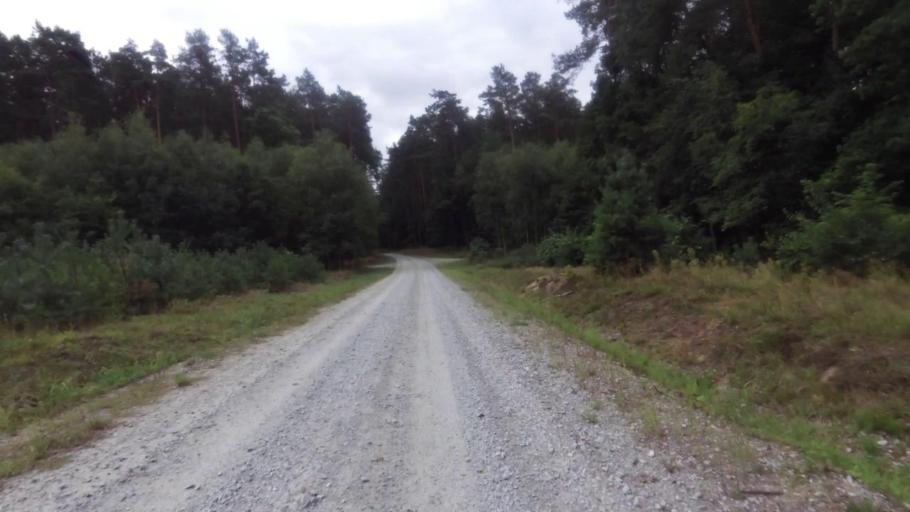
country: PL
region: Lubusz
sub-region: Powiat gorzowski
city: Kostrzyn nad Odra
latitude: 52.6511
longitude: 14.6385
